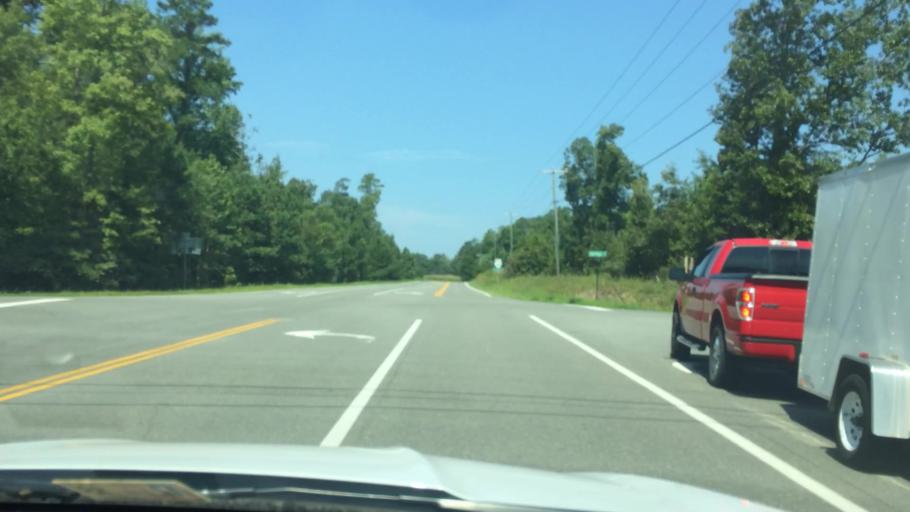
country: US
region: Virginia
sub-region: New Kent County
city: New Kent
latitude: 37.5235
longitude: -77.0084
